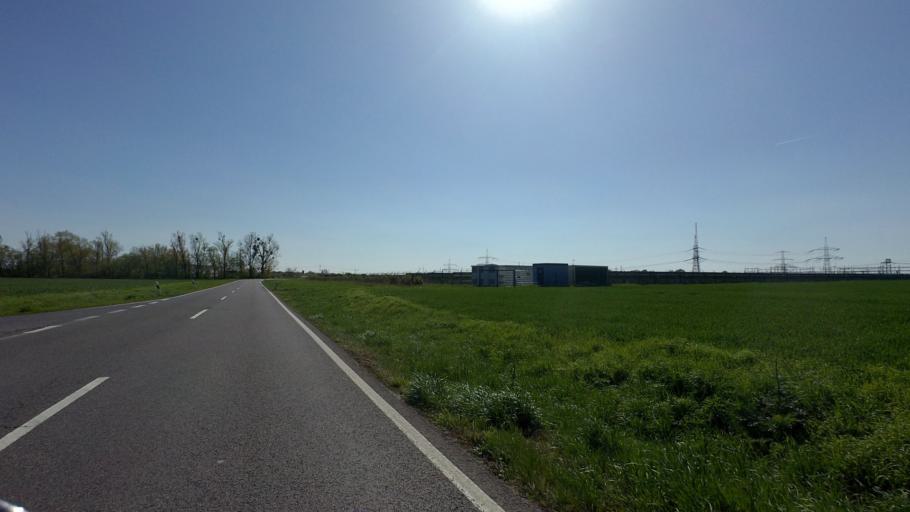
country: DE
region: Brandenburg
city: Wustermark
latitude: 52.5625
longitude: 12.9556
